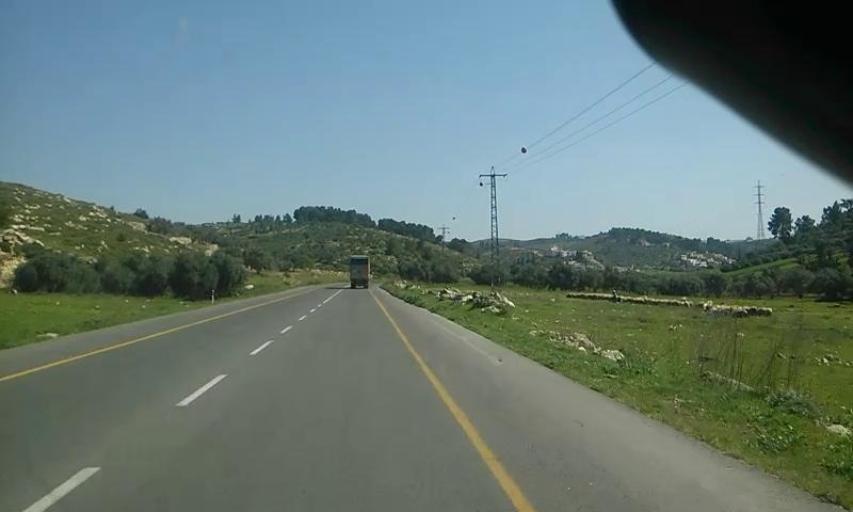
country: PS
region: West Bank
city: Idhna
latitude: 31.5746
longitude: 34.9814
